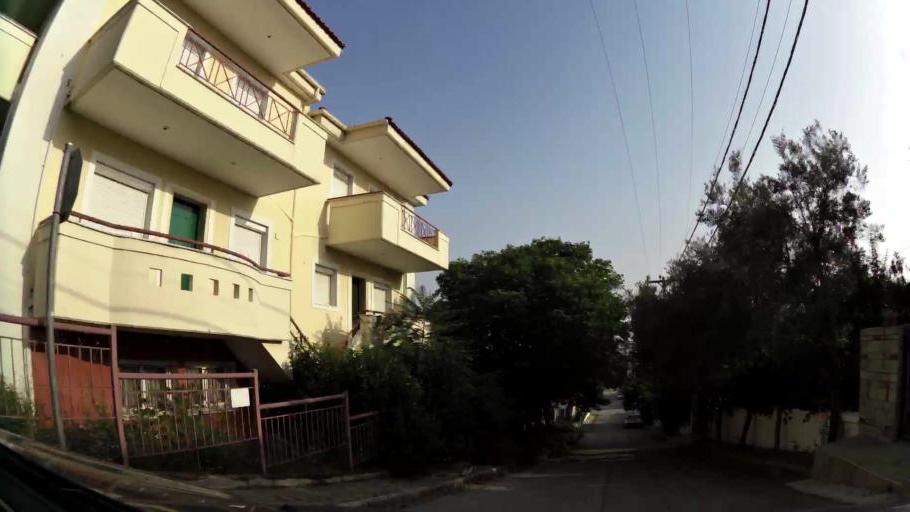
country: GR
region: Central Macedonia
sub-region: Nomos Thessalonikis
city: Oraiokastro
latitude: 40.7252
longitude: 22.9065
